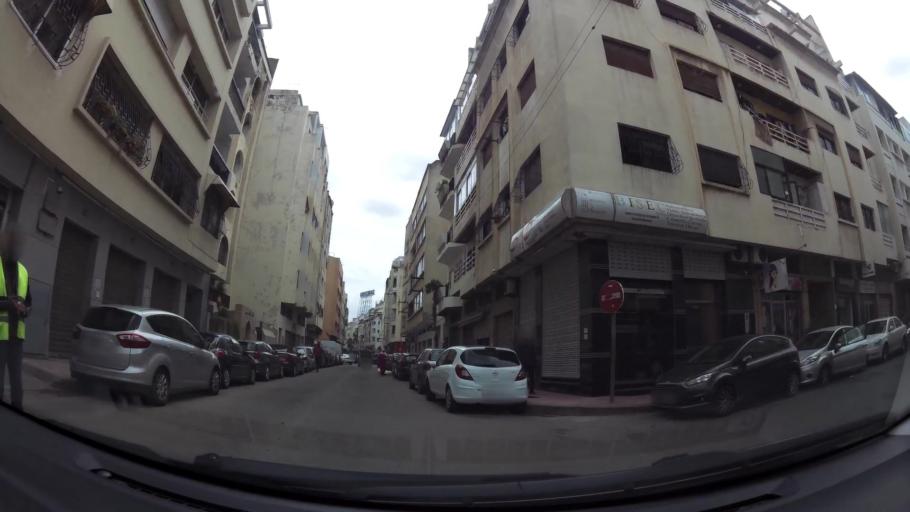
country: MA
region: Grand Casablanca
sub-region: Casablanca
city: Casablanca
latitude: 33.5722
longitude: -7.6460
